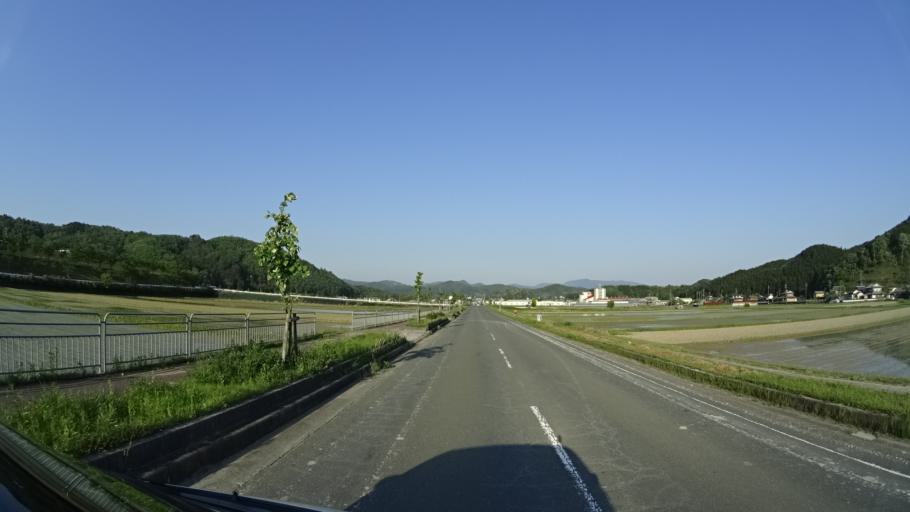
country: JP
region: Kyoto
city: Kameoka
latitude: 35.1082
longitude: 135.4453
